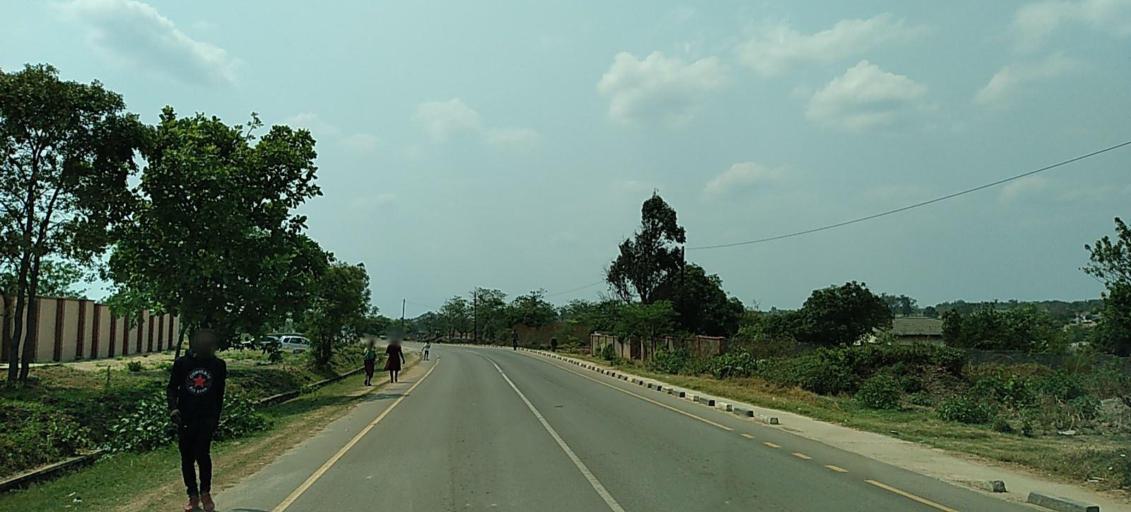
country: ZM
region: Copperbelt
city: Chambishi
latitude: -12.6388
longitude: 28.0596
